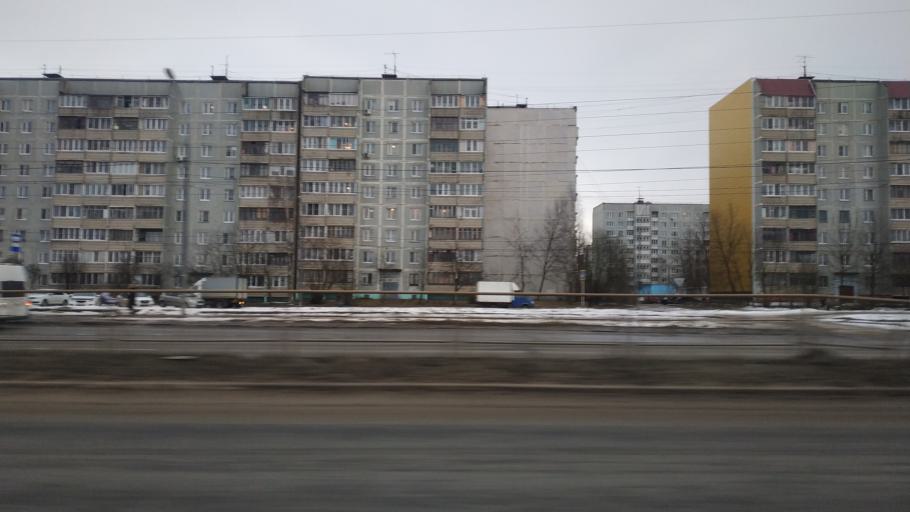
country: RU
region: Tverskaya
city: Tver
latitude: 56.8209
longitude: 35.8878
